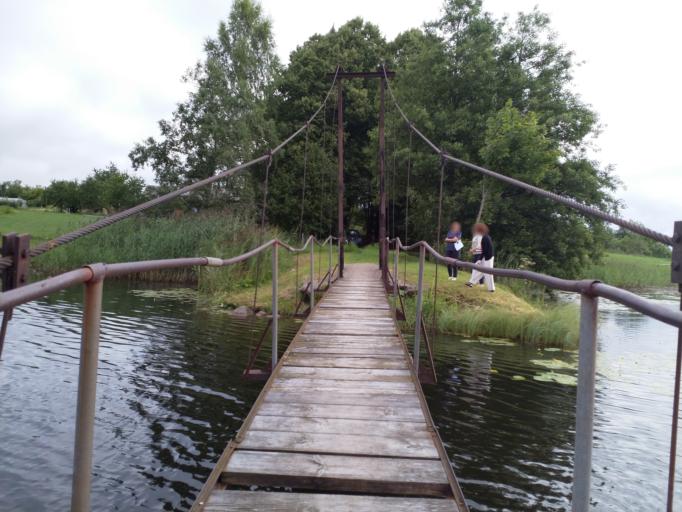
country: LV
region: Kuldigas Rajons
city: Kuldiga
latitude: 57.0154
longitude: 21.9058
